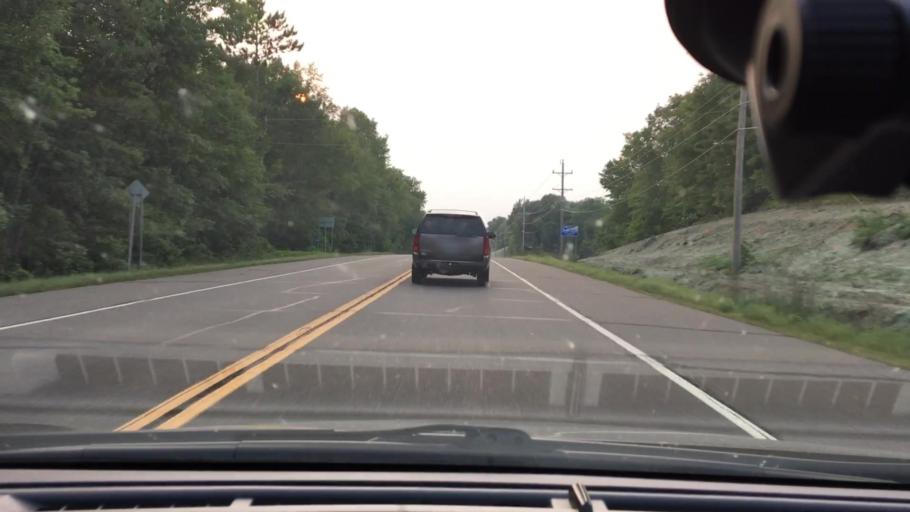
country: US
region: Minnesota
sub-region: Crow Wing County
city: Crosby
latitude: 46.4871
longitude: -93.9019
